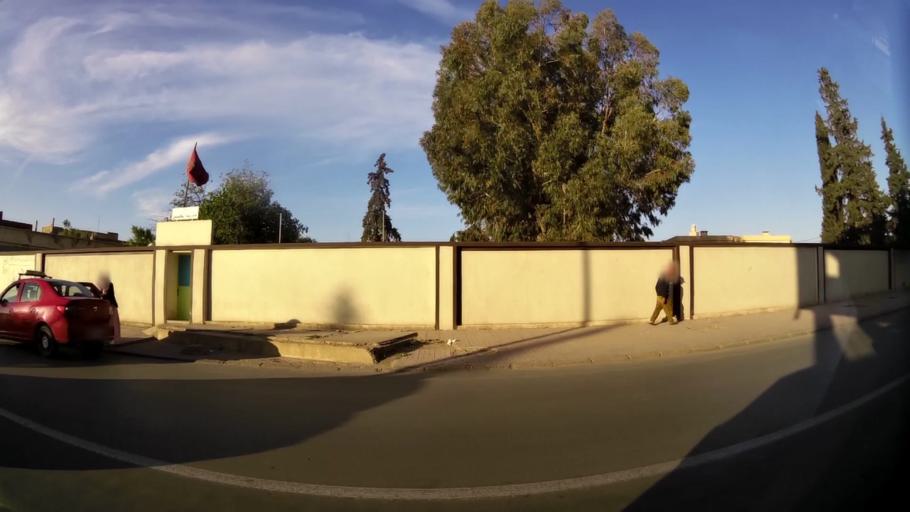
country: MA
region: Oriental
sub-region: Oujda-Angad
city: Oujda
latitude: 34.6993
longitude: -1.9108
